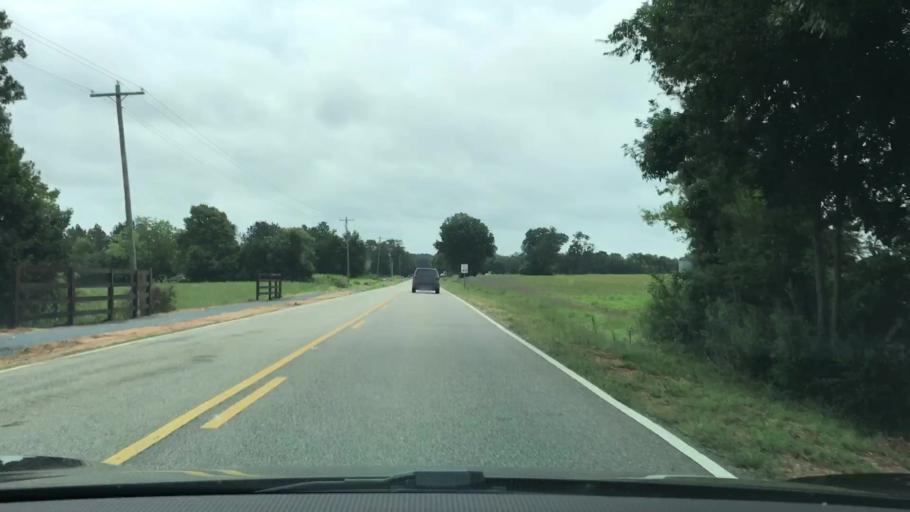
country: US
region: Alabama
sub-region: Montgomery County
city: Pike Road
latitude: 32.3015
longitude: -86.0690
